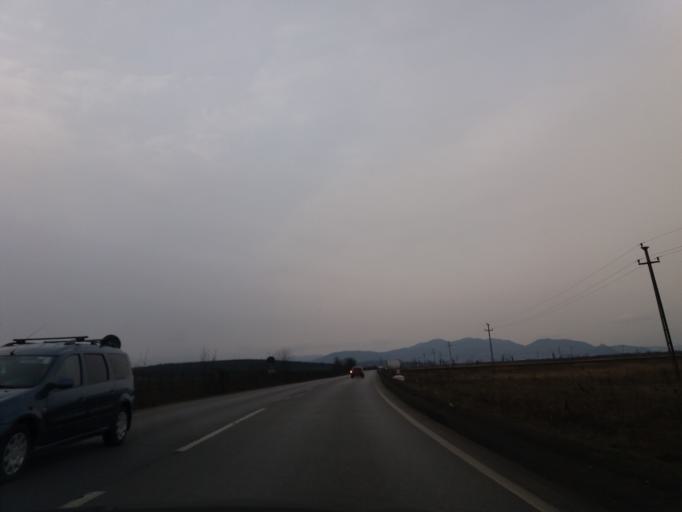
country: RO
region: Hunedoara
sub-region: Oras Simeria
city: Simeria
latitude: 45.8478
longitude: 23.0011
